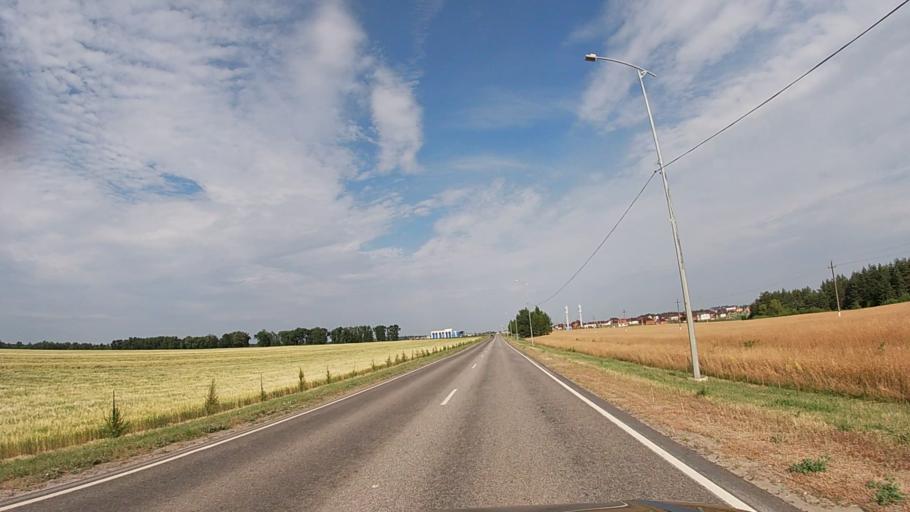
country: RU
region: Belgorod
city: Krasnaya Yaruga
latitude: 50.7961
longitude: 35.7026
